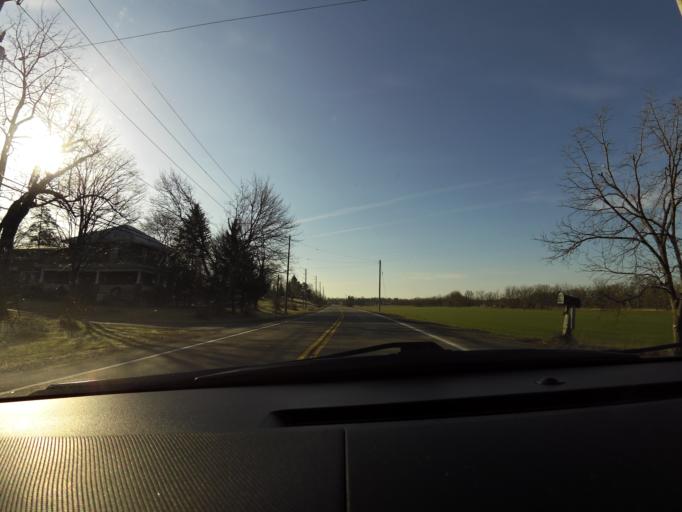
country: CA
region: Ontario
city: Ancaster
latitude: 43.0356
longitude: -79.8971
